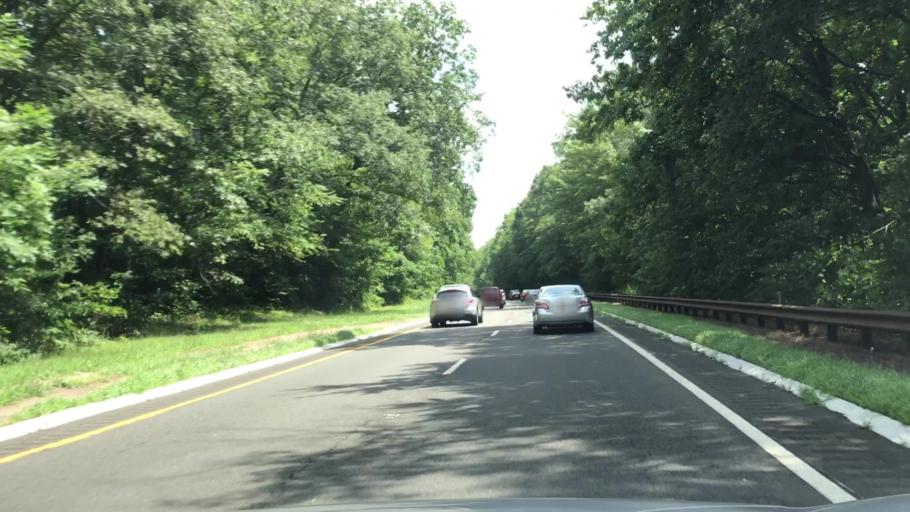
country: US
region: New York
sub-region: Rockland County
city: New Square
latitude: 41.1285
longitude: -74.0152
